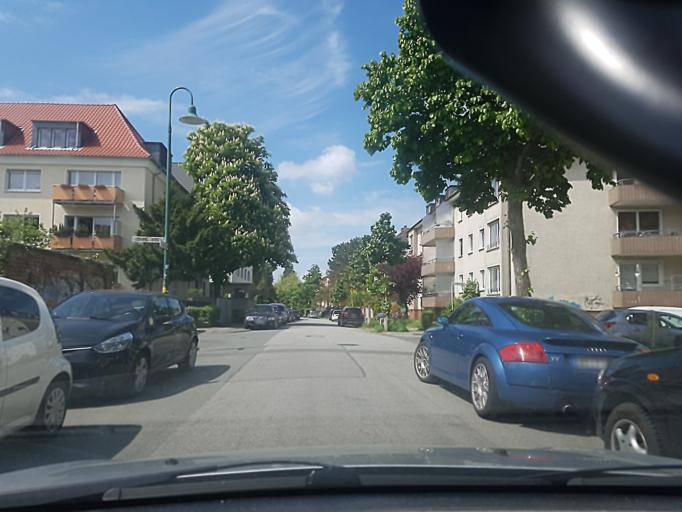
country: DE
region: Hesse
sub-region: Regierungsbezirk Darmstadt
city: Darmstadt
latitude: 49.8655
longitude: 8.6630
